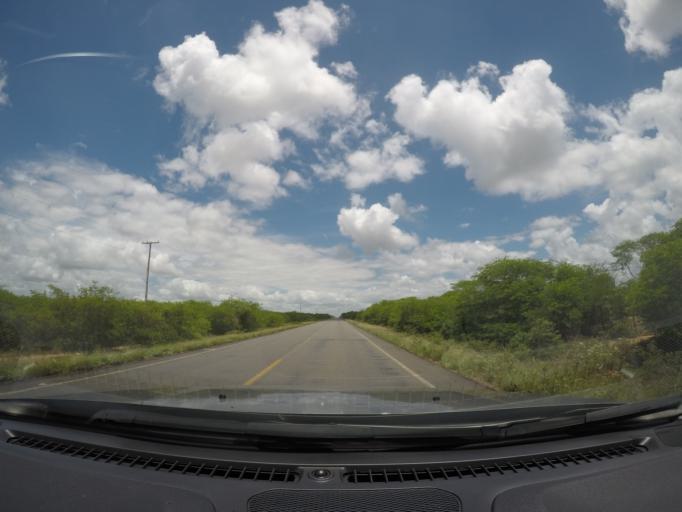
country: BR
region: Bahia
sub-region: Ipira
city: Ipira
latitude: -12.3505
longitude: -40.0086
